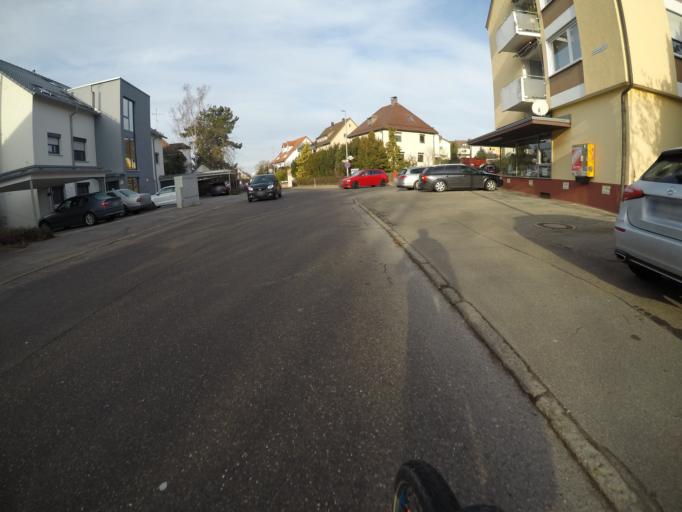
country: DE
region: Baden-Wuerttemberg
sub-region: Regierungsbezirk Stuttgart
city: Sindelfingen
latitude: 48.6904
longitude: 9.0231
